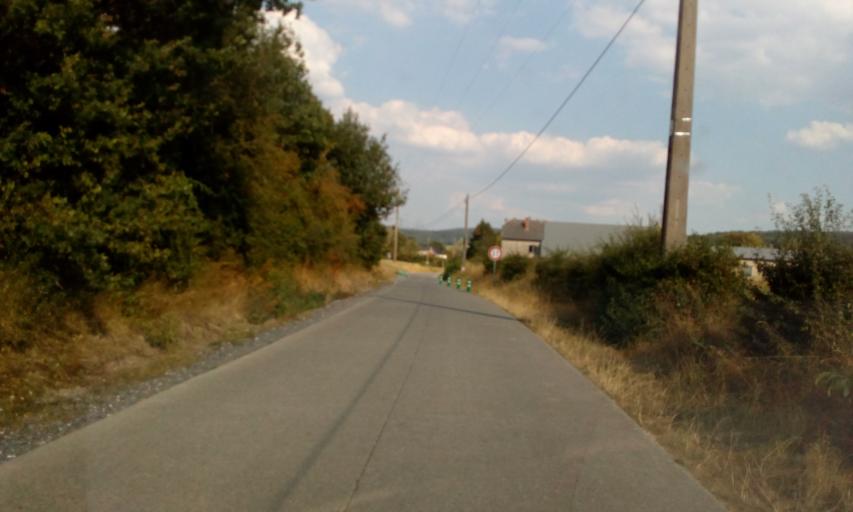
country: BE
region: Wallonia
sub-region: Province du Luxembourg
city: Tellin
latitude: 50.1087
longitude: 5.1858
